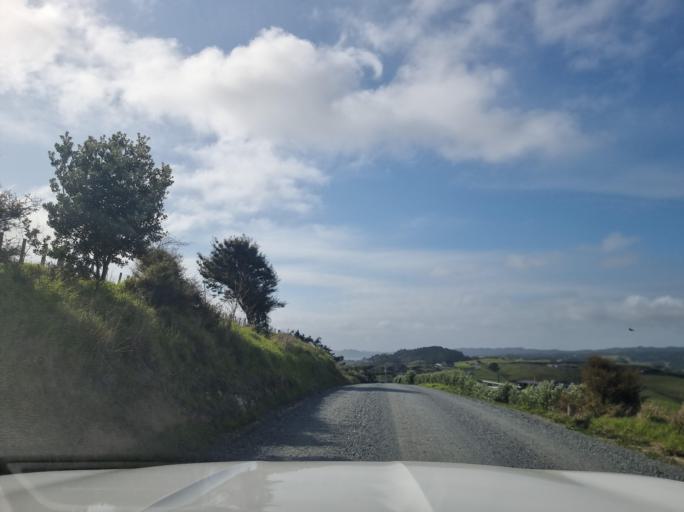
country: NZ
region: Northland
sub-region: Whangarei
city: Ruakaka
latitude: -36.0118
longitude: 174.4757
